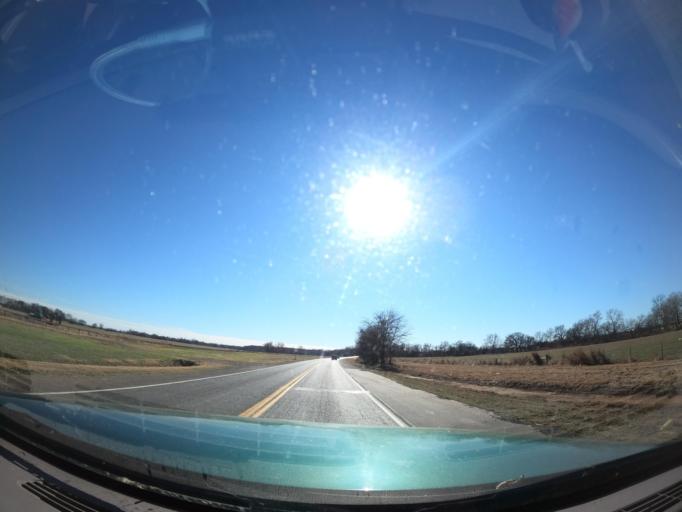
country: US
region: Oklahoma
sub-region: Muskogee County
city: Haskell
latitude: 35.8829
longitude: -95.6599
